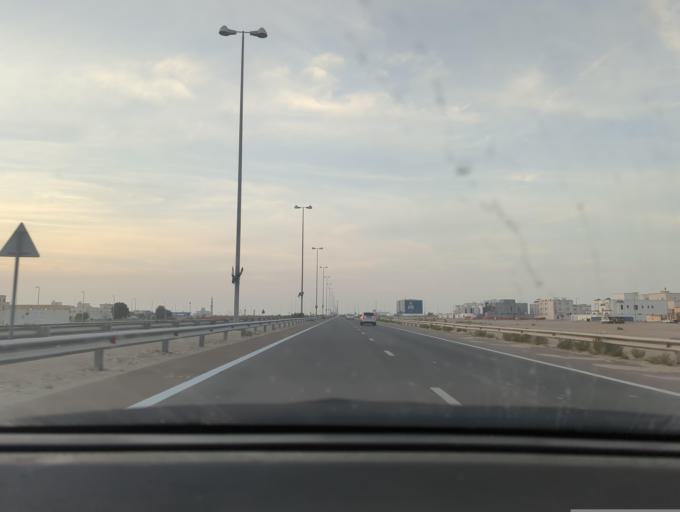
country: AE
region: Abu Dhabi
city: Abu Dhabi
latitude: 24.3321
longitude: 54.6478
